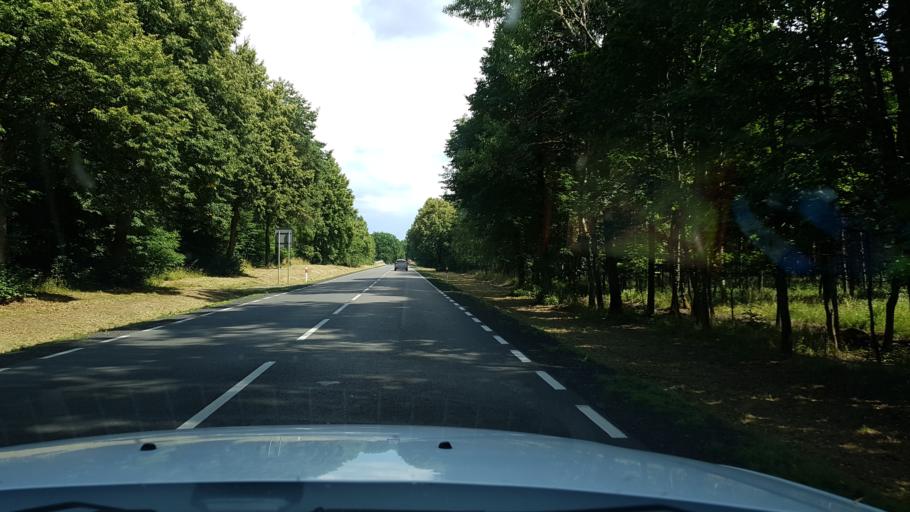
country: PL
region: West Pomeranian Voivodeship
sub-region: Powiat walecki
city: Walcz
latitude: 53.3087
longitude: 16.3877
